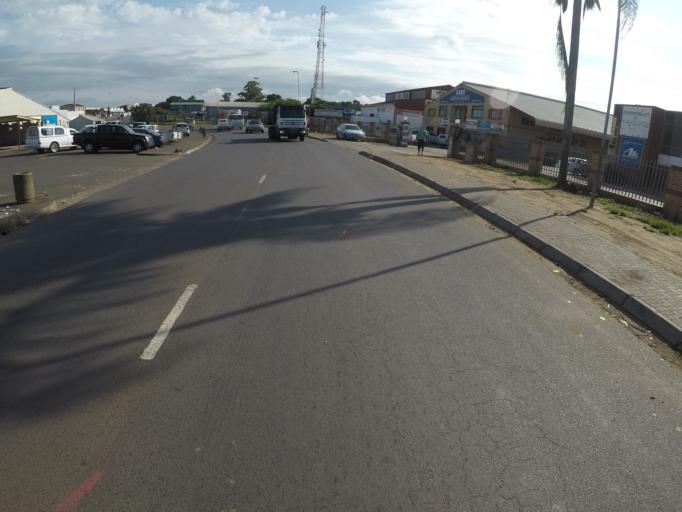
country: ZA
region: KwaZulu-Natal
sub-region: uThungulu District Municipality
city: Empangeni
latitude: -28.7706
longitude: 31.9055
